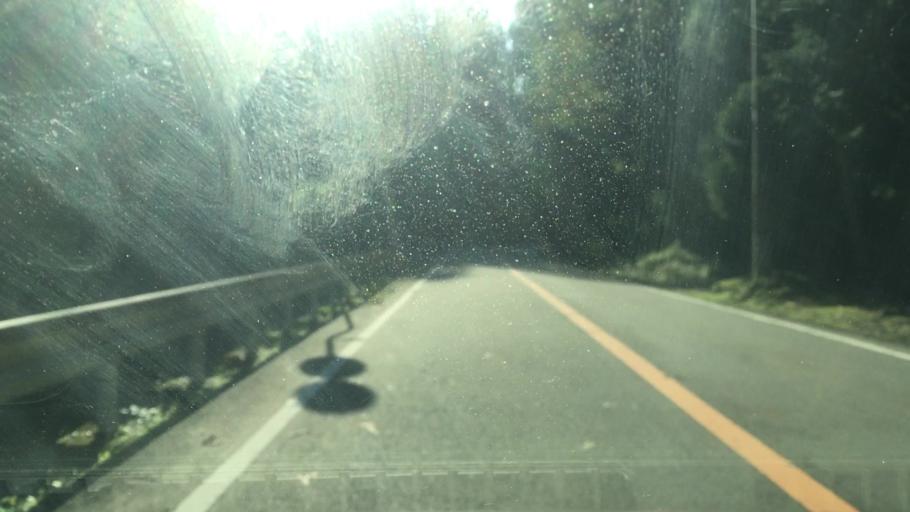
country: JP
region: Hyogo
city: Toyooka
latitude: 35.6168
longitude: 134.8558
